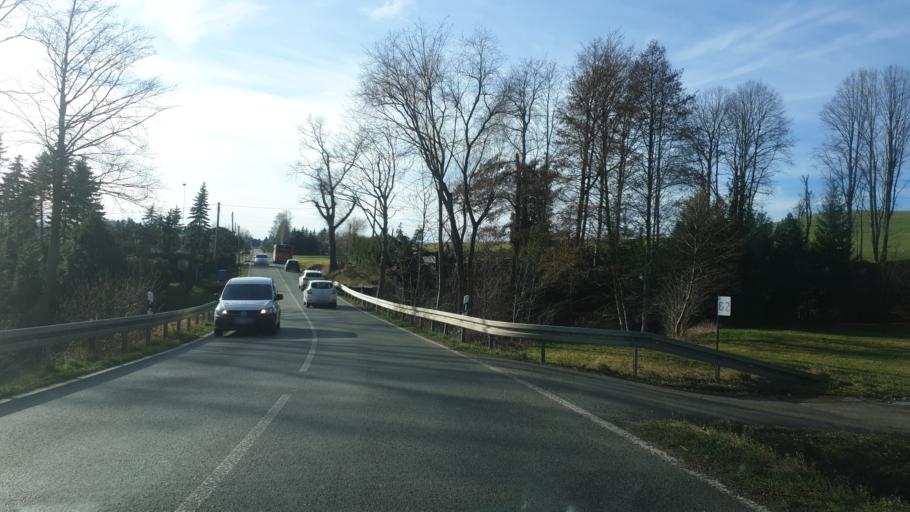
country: DE
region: Saxony
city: Wildenfels
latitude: 50.6664
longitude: 12.6328
